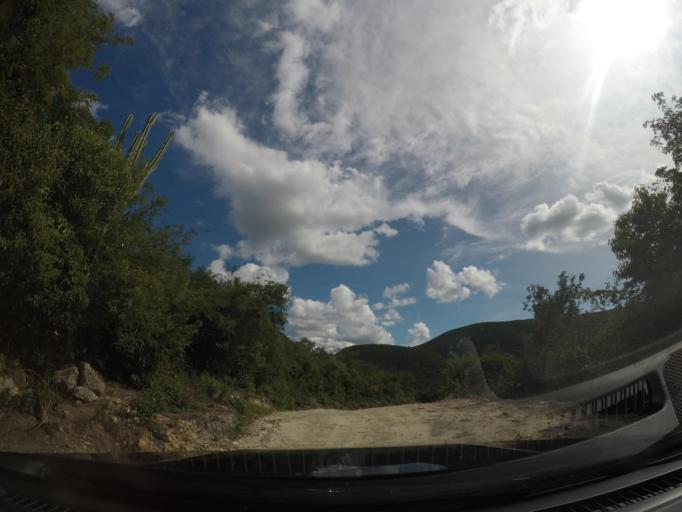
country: BR
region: Bahia
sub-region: Barra Da Estiva
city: Barra da Estiva
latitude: -13.1453
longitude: -41.5985
